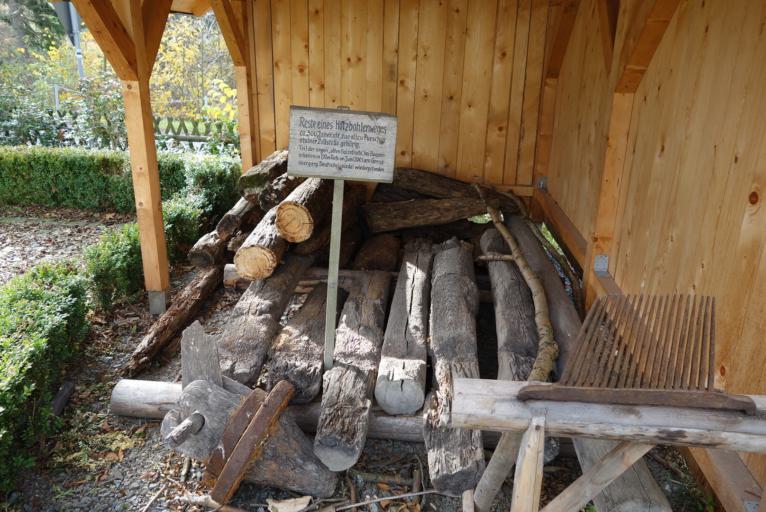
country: DE
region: Saxony
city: Neuhausen
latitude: 50.6772
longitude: 13.4621
